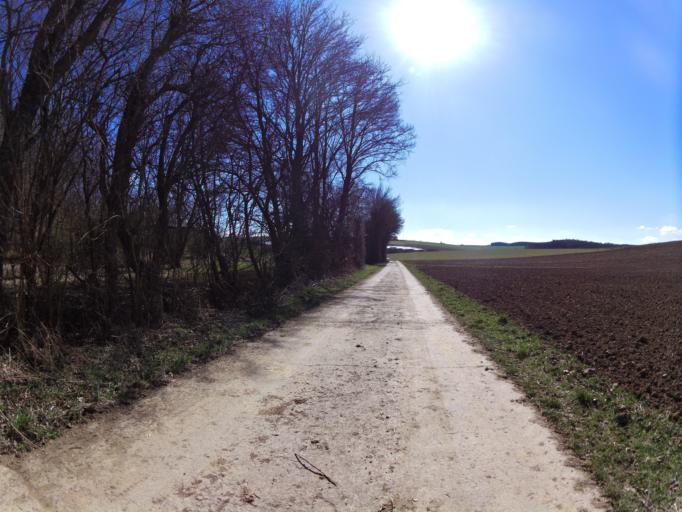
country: DE
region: Bavaria
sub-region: Regierungsbezirk Unterfranken
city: Hettstadt
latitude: 49.8043
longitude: 9.7945
